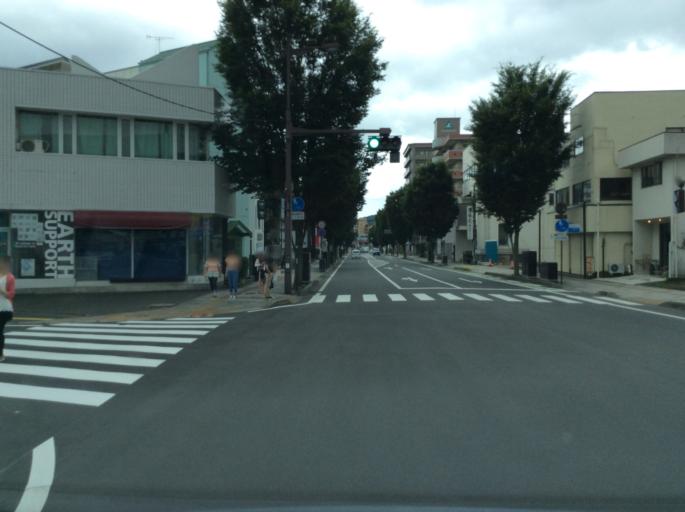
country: JP
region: Fukushima
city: Fukushima-shi
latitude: 37.7621
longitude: 140.4592
